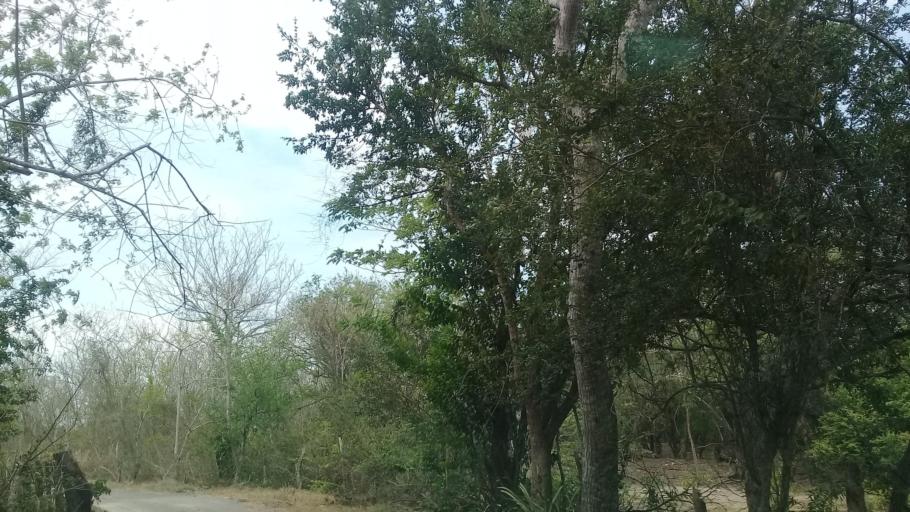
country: MX
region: Veracruz
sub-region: Veracruz
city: Delfino Victoria (Santa Fe)
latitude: 19.1756
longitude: -96.3038
